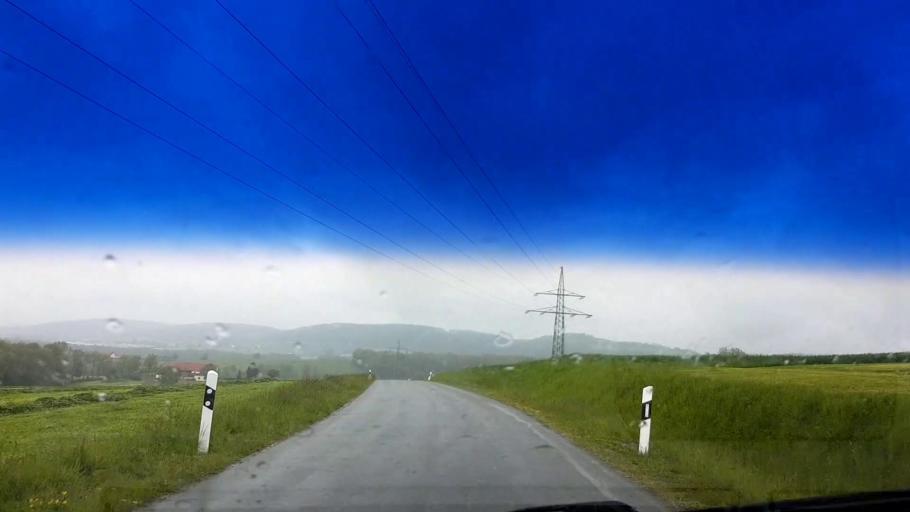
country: DE
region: Bavaria
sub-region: Upper Franconia
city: Gesees
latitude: 50.0246
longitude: 11.6263
